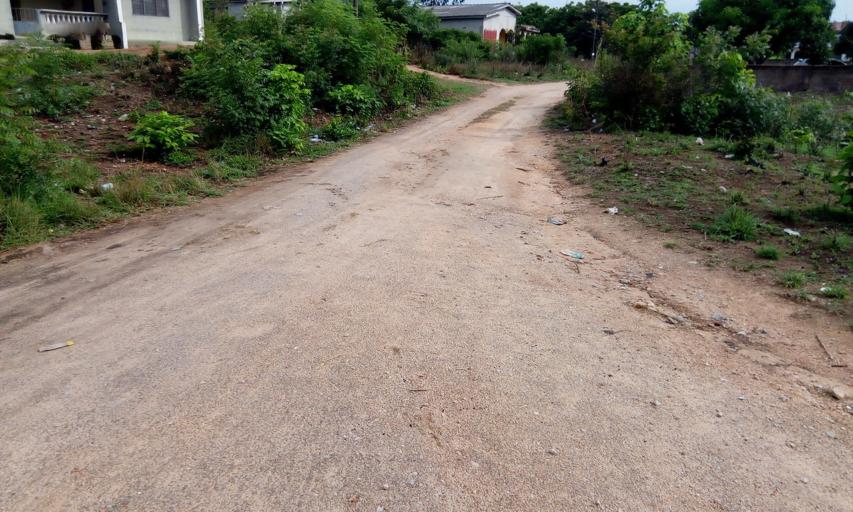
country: GH
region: Central
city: Winneba
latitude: 5.3602
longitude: -0.6202
